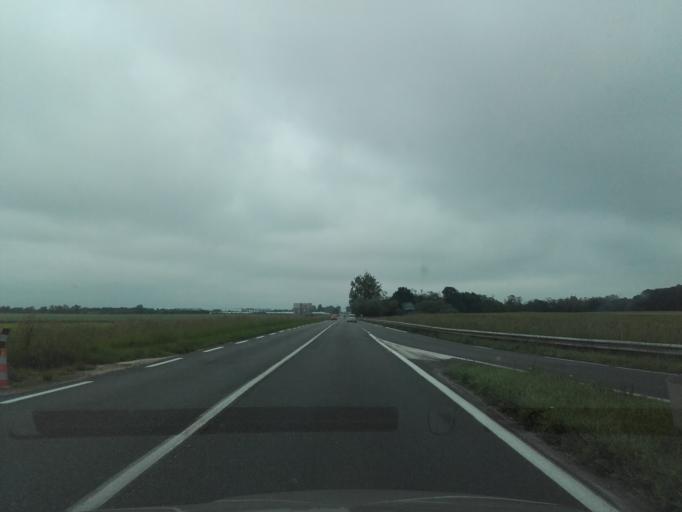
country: FR
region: Centre
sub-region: Departement d'Indre-et-Loire
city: Parcay-Meslay
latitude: 47.4553
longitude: 0.7348
